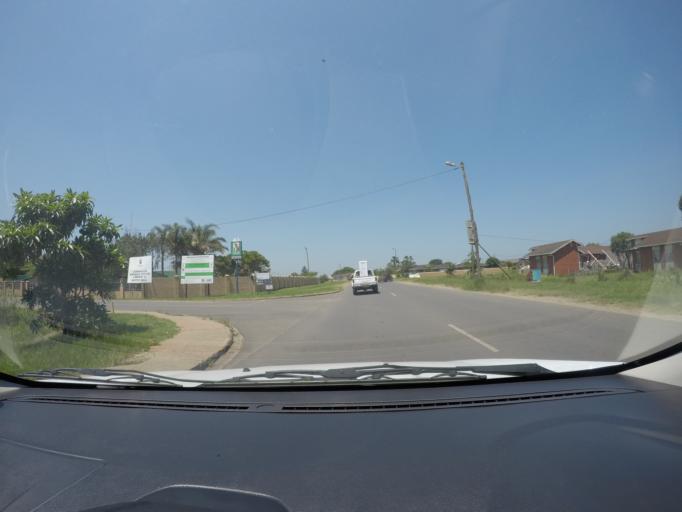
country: ZA
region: KwaZulu-Natal
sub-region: uThungulu District Municipality
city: eSikhawini
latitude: -28.8694
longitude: 31.9091
